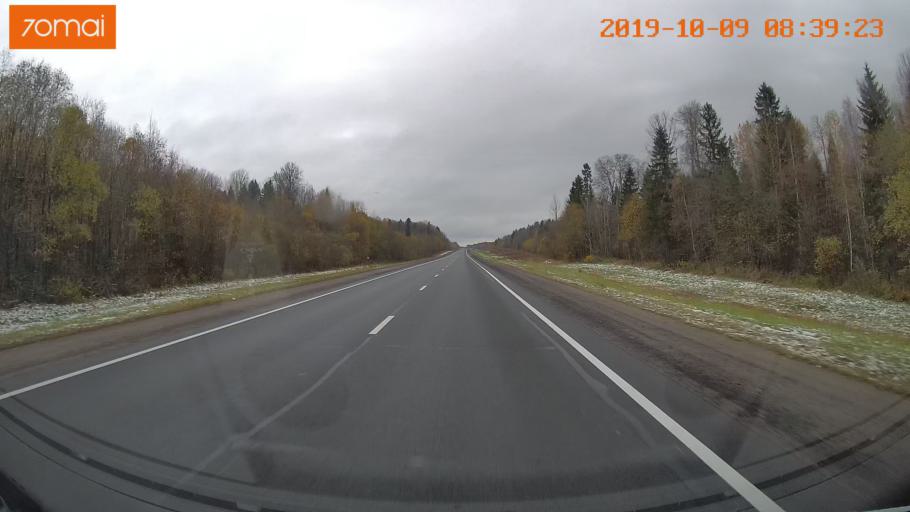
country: RU
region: Vologda
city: Gryazovets
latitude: 58.9703
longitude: 40.1533
